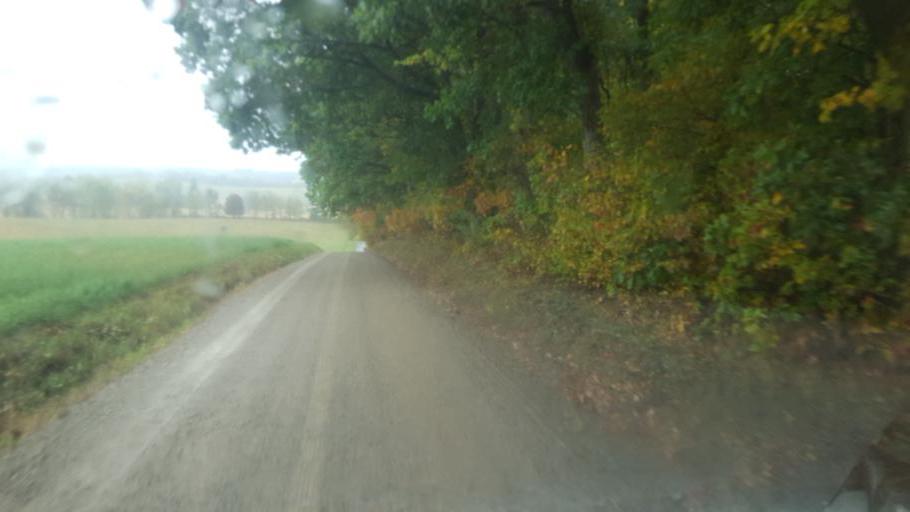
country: US
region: Ohio
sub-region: Knox County
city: Danville
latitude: 40.4926
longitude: -82.3064
